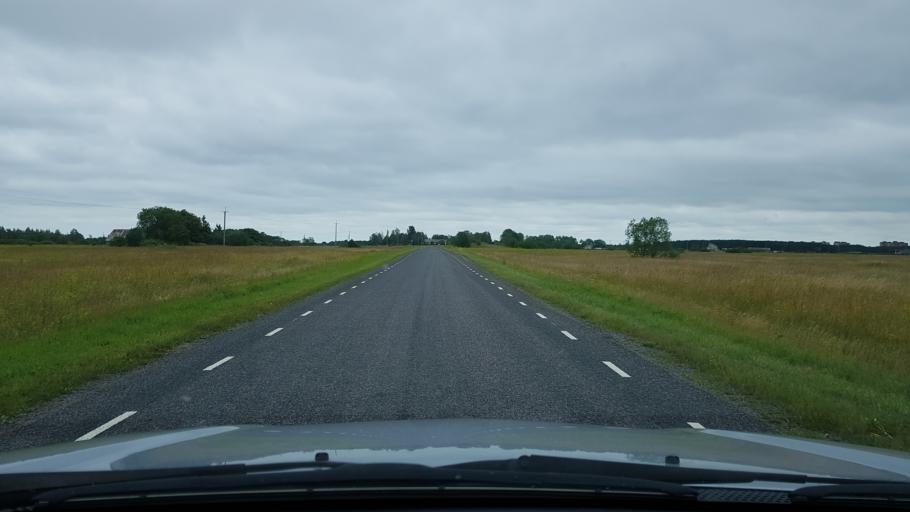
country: EE
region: Ida-Virumaa
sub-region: Narva linn
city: Narva
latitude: 59.3798
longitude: 28.1262
